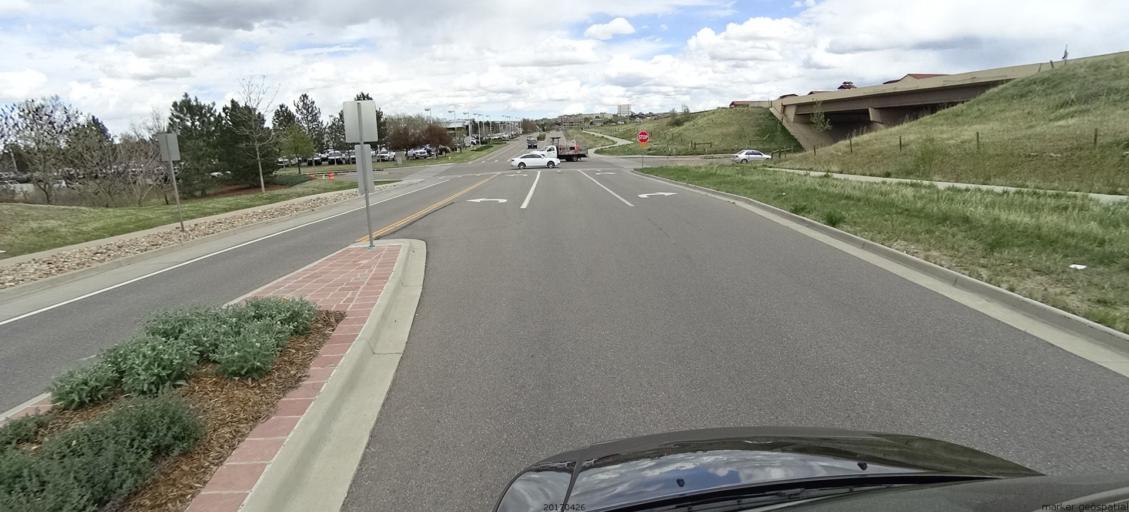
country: US
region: Colorado
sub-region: Douglas County
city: Acres Green
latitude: 39.5647
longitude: -104.8978
